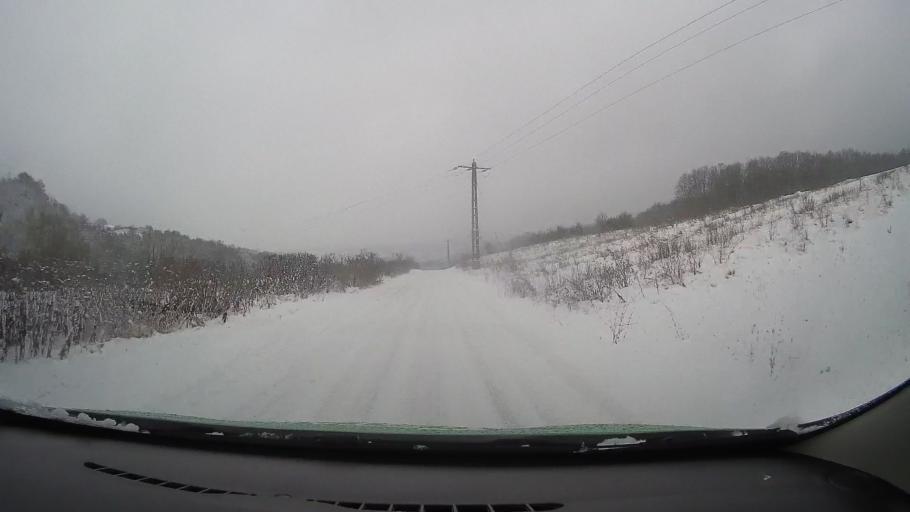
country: RO
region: Hunedoara
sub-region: Comuna Carjiti
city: Carjiti
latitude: 45.8388
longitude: 22.8365
